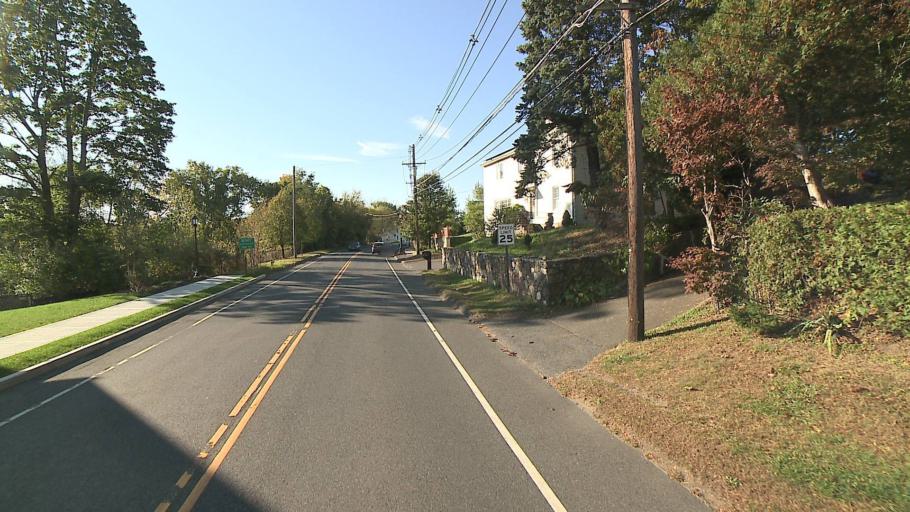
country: US
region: Connecticut
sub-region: Fairfield County
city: Bethel
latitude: 41.3812
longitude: -73.4250
